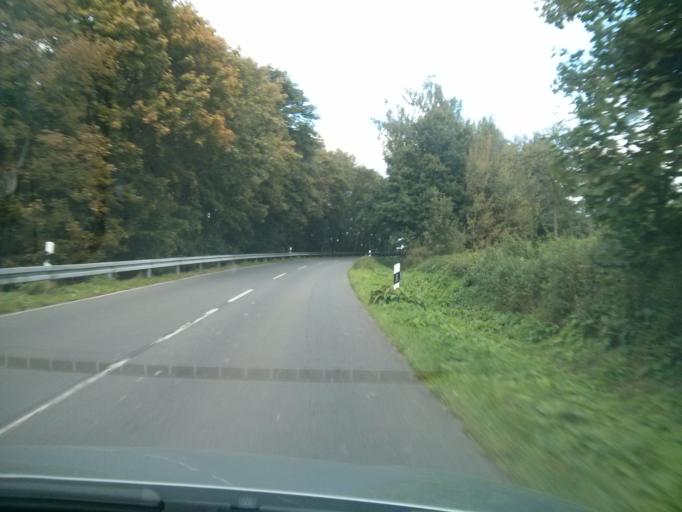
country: DE
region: North Rhine-Westphalia
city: Wickede
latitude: 51.4894
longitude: 7.9246
